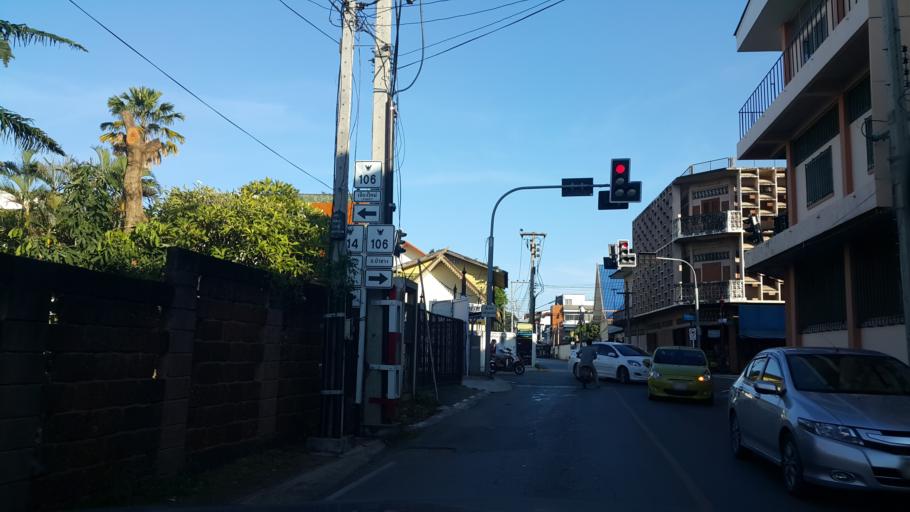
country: TH
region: Lamphun
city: Lamphun
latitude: 18.5769
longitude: 99.0064
